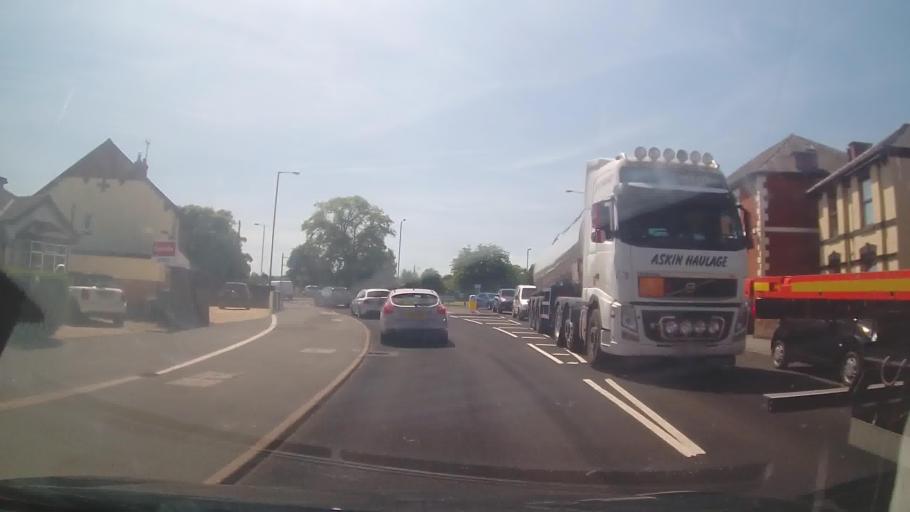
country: GB
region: England
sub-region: Herefordshire
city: Hereford
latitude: 52.0666
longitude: -2.7217
